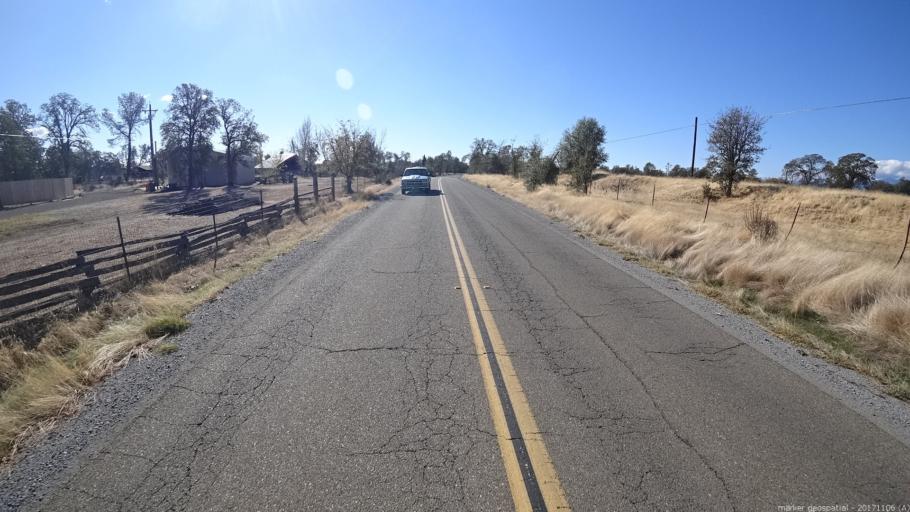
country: US
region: California
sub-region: Shasta County
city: Bella Vista
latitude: 40.6068
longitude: -122.2777
